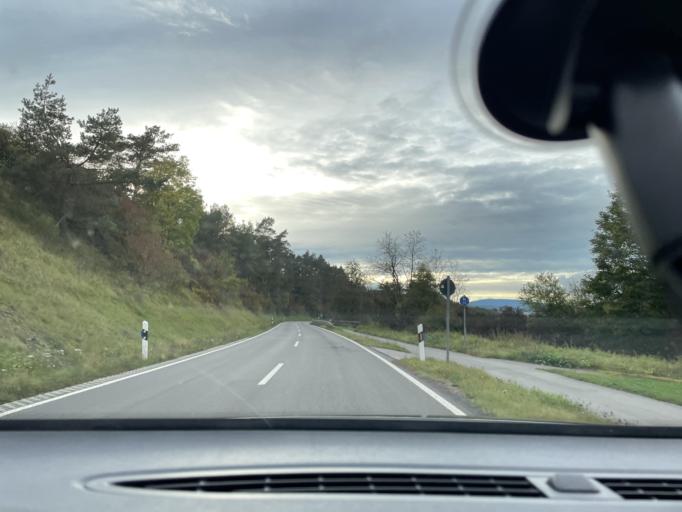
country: DE
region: Bavaria
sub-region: Regierungsbezirk Unterfranken
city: Strahlungen
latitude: 50.3075
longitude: 10.2417
